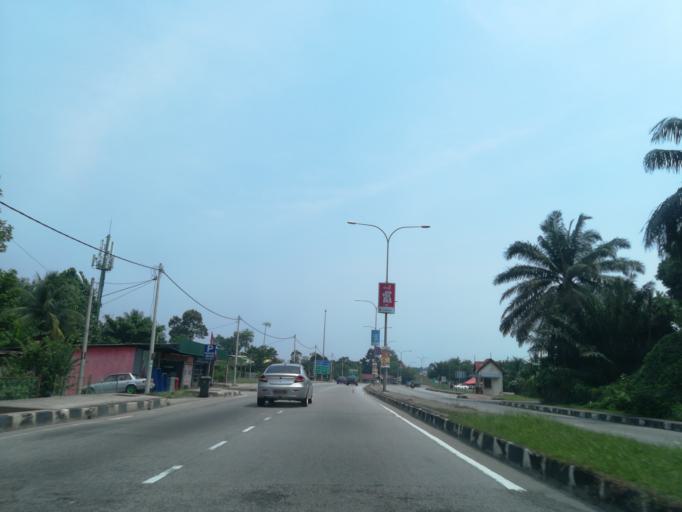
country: MY
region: Kedah
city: Kulim
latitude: 5.4174
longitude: 100.5390
